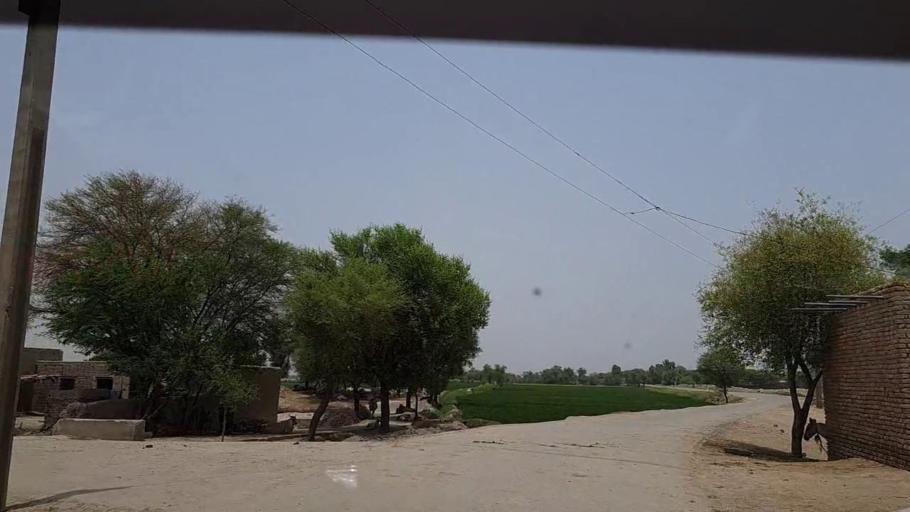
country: PK
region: Sindh
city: Khairpur Nathan Shah
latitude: 27.0179
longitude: 67.6691
